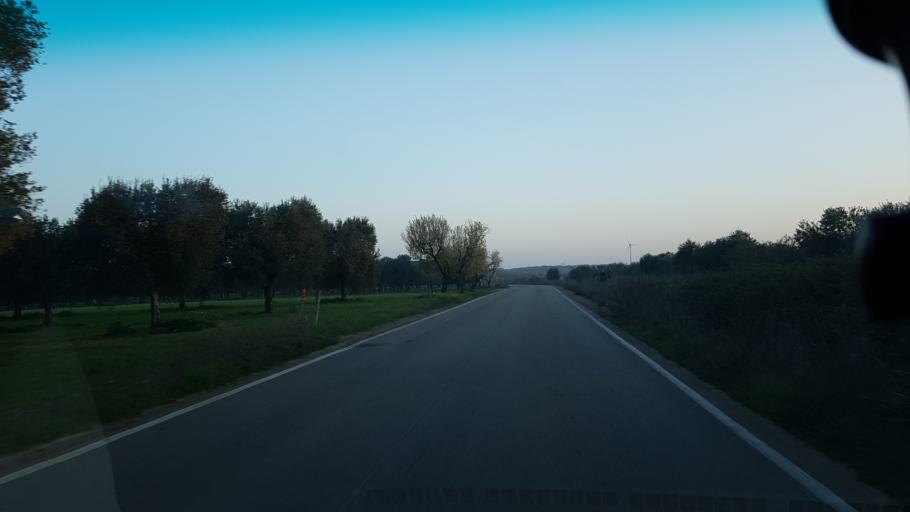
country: IT
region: Apulia
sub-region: Provincia di Brindisi
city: Mesagne
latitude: 40.6236
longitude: 17.7839
